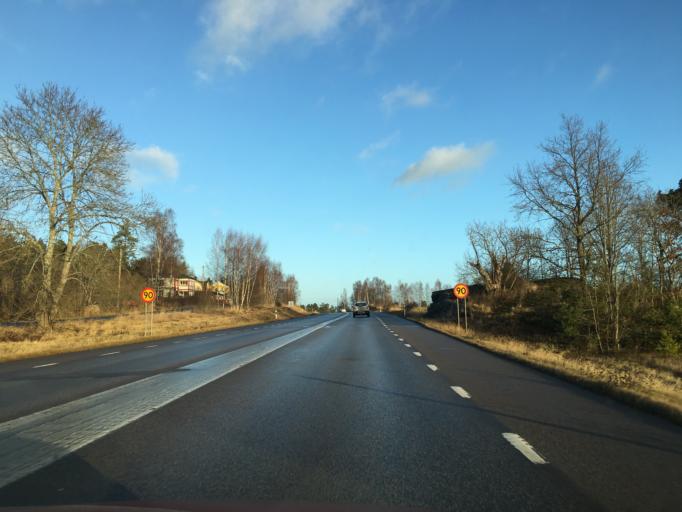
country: SE
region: Kalmar
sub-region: Vasterviks Kommun
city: Ankarsrum
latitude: 57.7116
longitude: 16.4491
